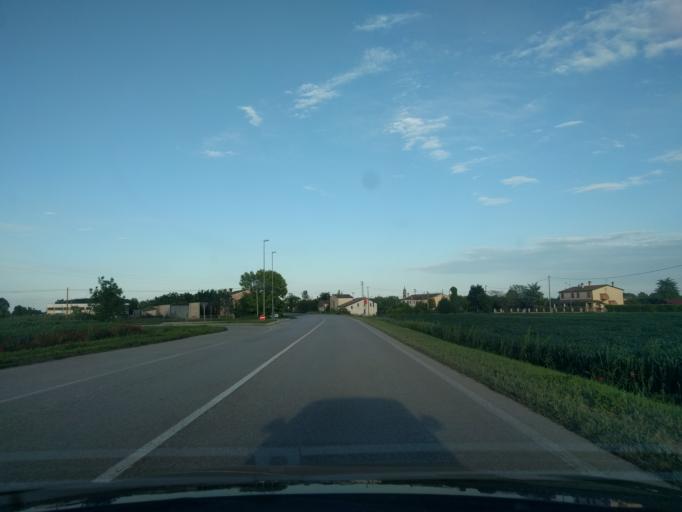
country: IT
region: Veneto
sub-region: Provincia di Rovigo
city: Crespino
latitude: 44.9873
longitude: 11.8741
